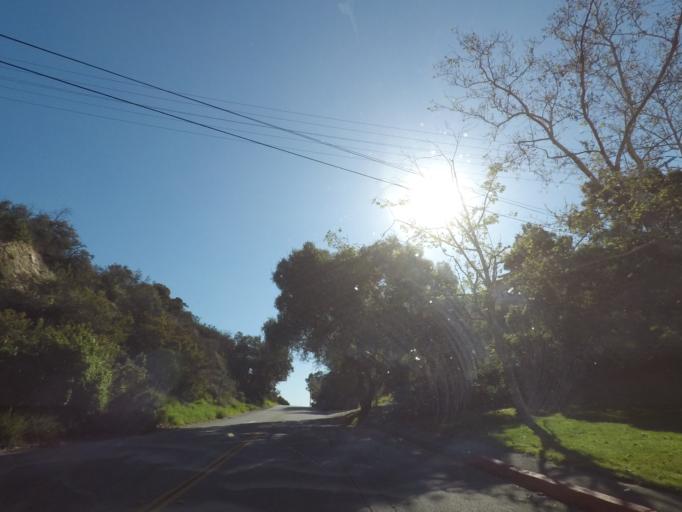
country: US
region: California
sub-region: Los Angeles County
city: La Canada Flintridge
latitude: 34.1720
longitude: -118.1917
